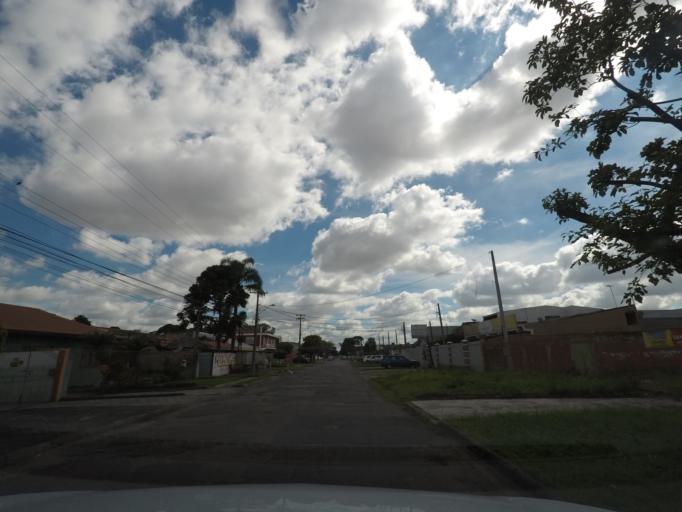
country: BR
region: Parana
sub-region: Sao Jose Dos Pinhais
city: Sao Jose dos Pinhais
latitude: -25.5043
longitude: -49.2265
